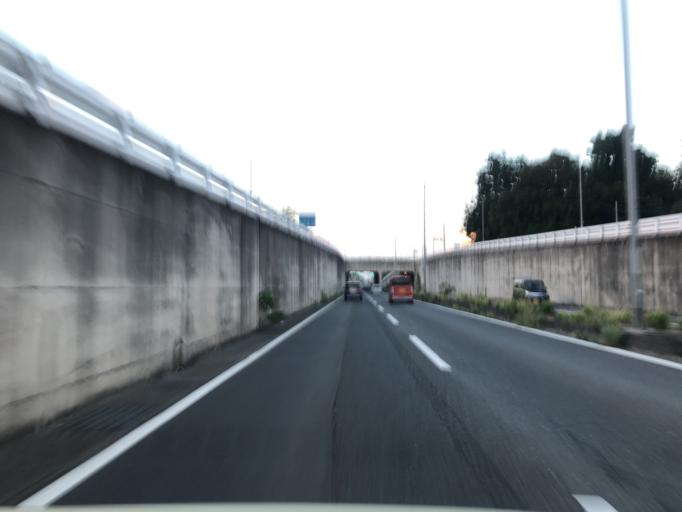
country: JP
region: Saitama
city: Sakado
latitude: 36.0220
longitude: 139.4128
